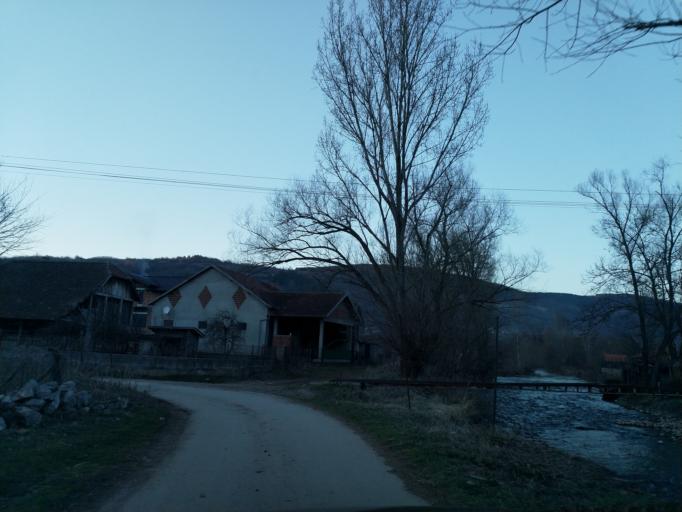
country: RS
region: Central Serbia
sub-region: Pomoravski Okrug
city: Paracin
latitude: 43.9307
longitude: 21.5206
